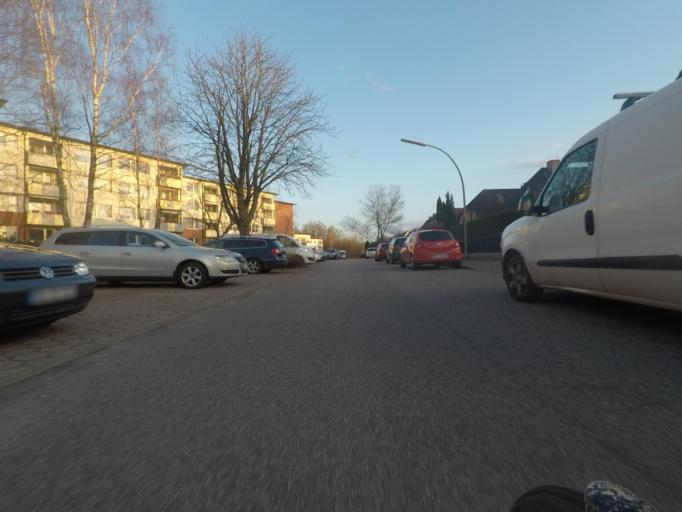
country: DE
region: Schleswig-Holstein
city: Barsbuettel
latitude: 53.6136
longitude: 10.1686
